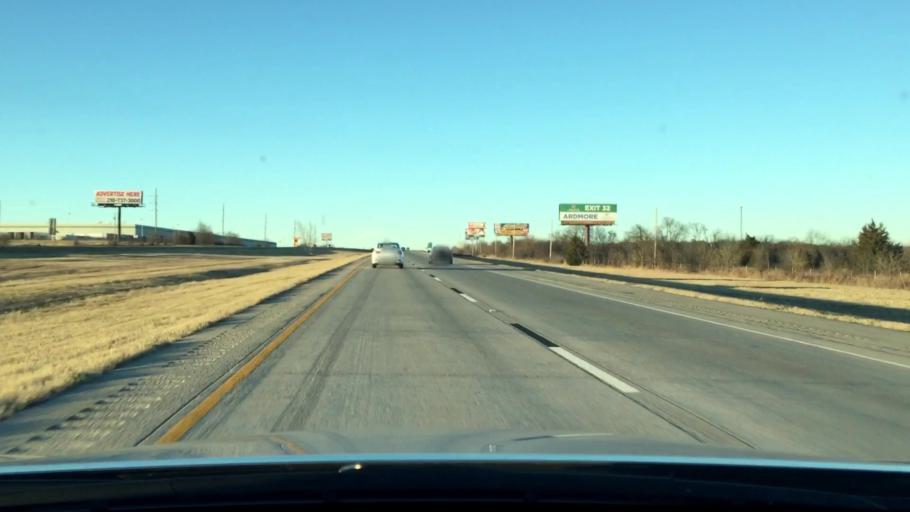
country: US
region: Oklahoma
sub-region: Love County
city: Marietta
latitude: 33.9287
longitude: -97.1345
